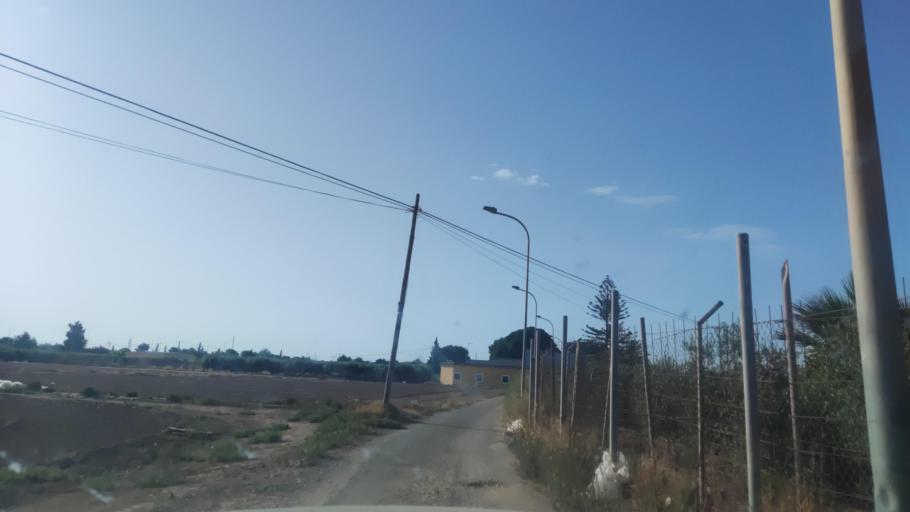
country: ES
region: Murcia
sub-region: Murcia
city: San Javier
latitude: 37.8096
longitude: -0.8555
